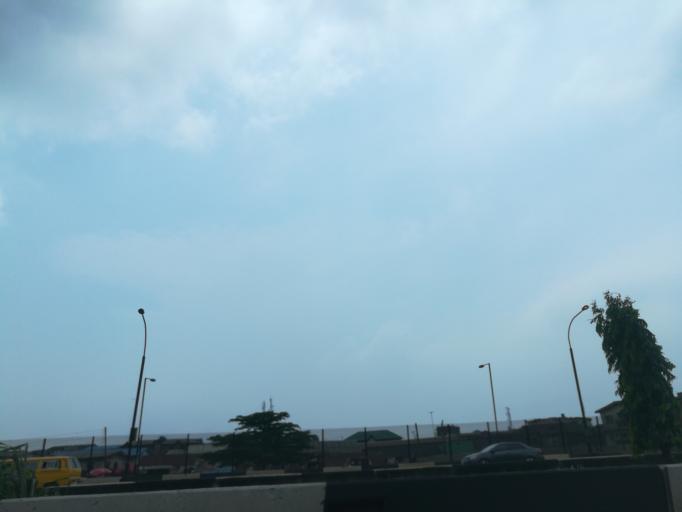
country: NG
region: Lagos
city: Somolu
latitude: 6.5532
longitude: 3.3968
